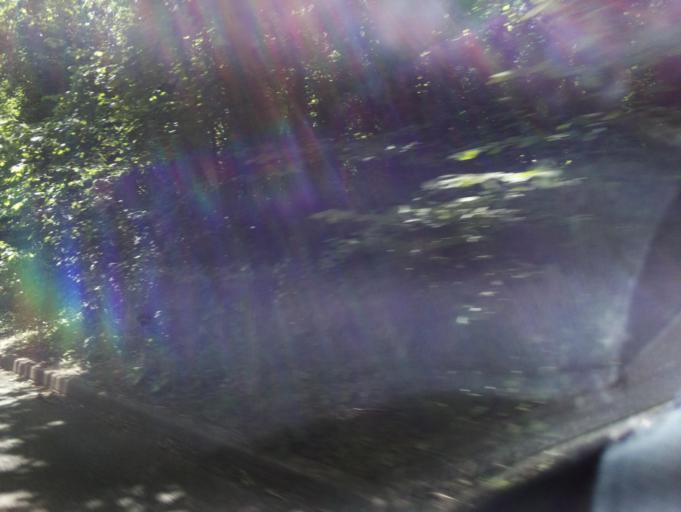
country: GB
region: Wales
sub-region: Monmouthshire
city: Caldicot
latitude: 51.6218
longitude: -2.7329
